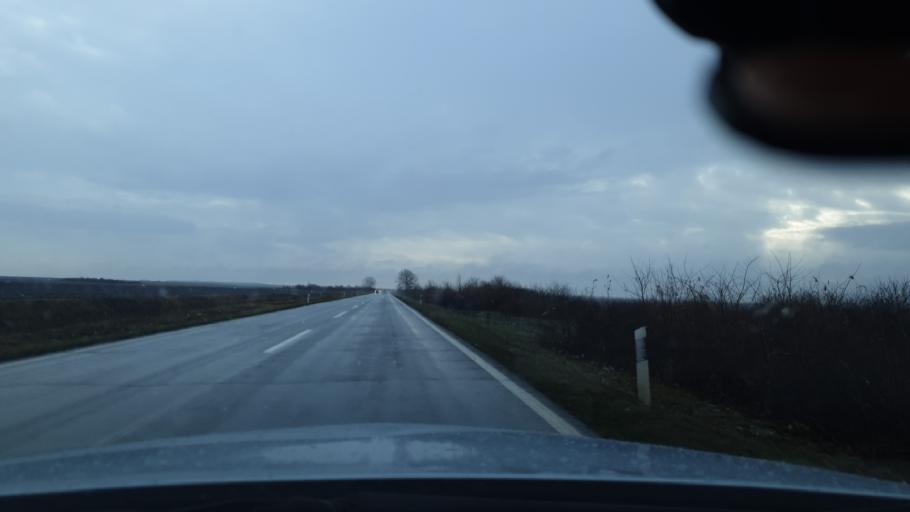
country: RS
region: Autonomna Pokrajina Vojvodina
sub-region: Juznobanatski Okrug
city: Pancevo
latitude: 44.8407
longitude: 20.7994
